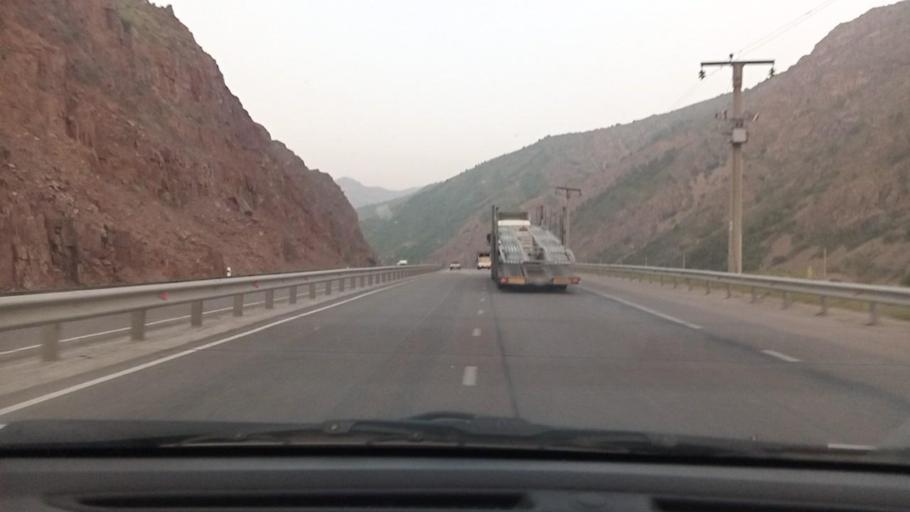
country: UZ
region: Toshkent
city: Angren
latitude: 41.1404
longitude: 70.3909
